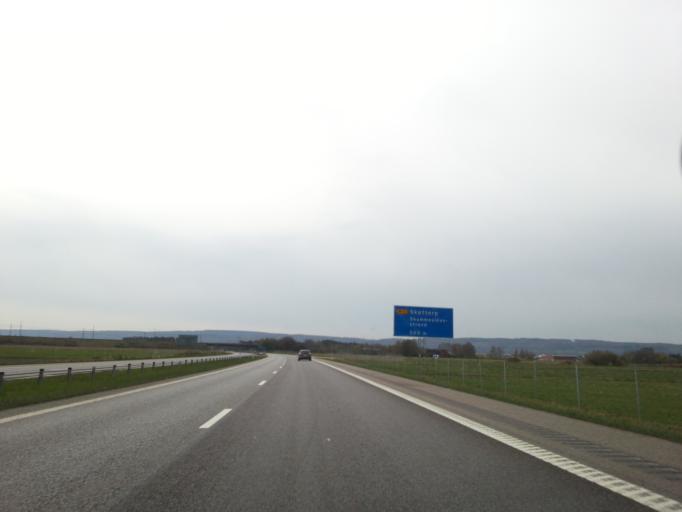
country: SE
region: Halland
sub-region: Laholms Kommun
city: Mellbystrand
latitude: 56.4630
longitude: 12.9416
